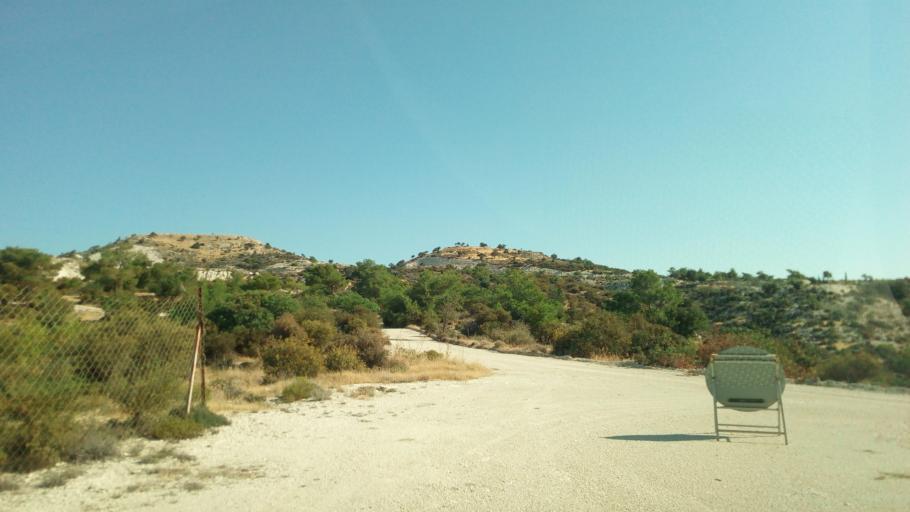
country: CY
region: Larnaka
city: Kofinou
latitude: 34.8078
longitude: 33.3151
